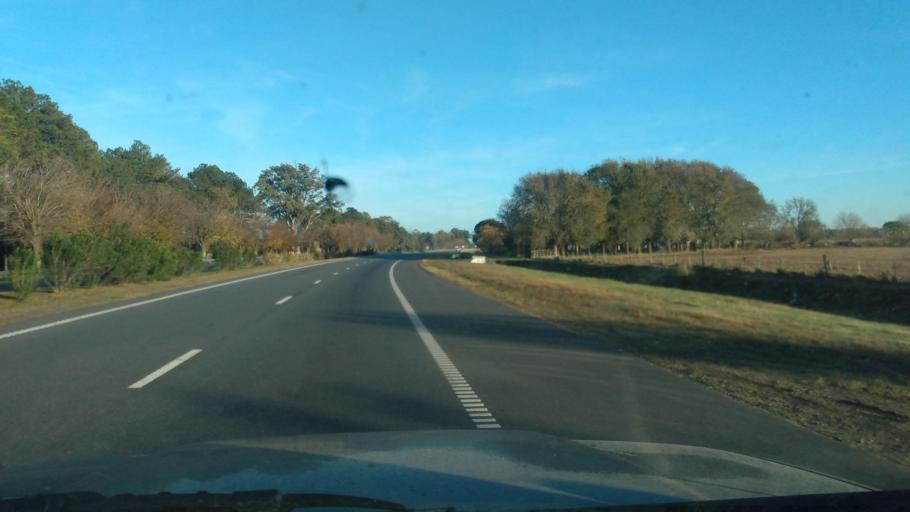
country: AR
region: Buenos Aires
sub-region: Partido de Lujan
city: Lujan
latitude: -34.5430
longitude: -59.2385
